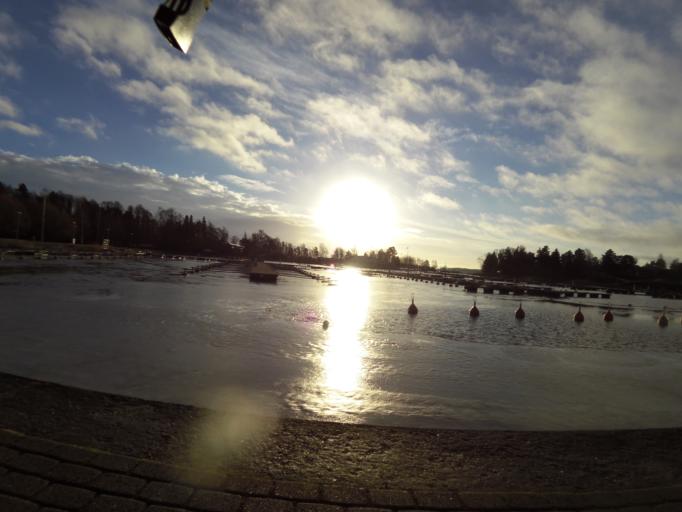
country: FI
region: Uusimaa
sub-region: Helsinki
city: Koukkuniemi
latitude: 60.1578
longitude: 24.7702
